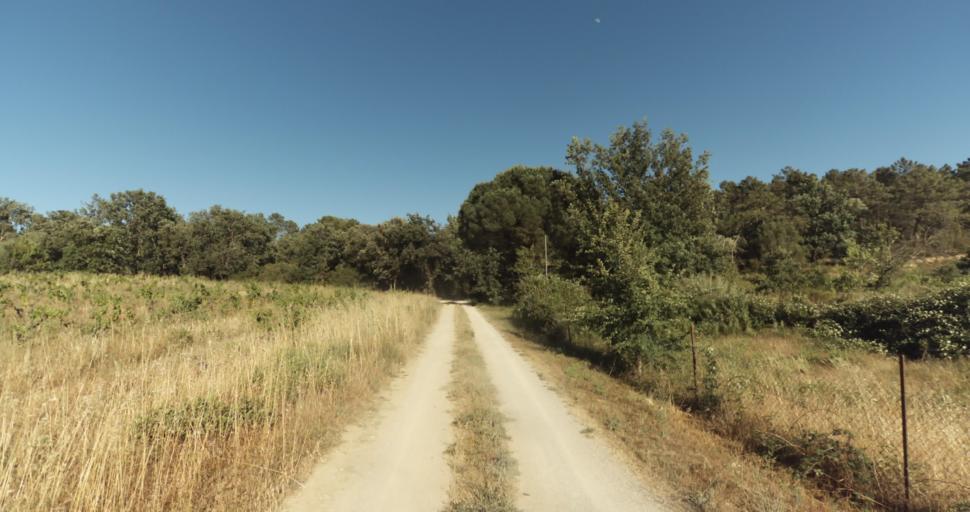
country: FR
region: Provence-Alpes-Cote d'Azur
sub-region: Departement du Var
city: Gassin
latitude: 43.2480
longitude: 6.5954
